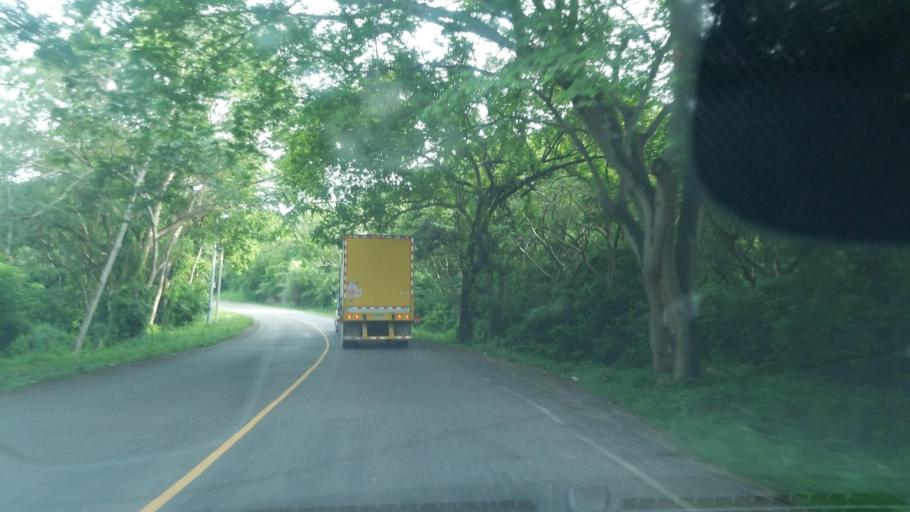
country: HN
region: Santa Barbara
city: Ilama
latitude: 15.0745
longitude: -88.2252
